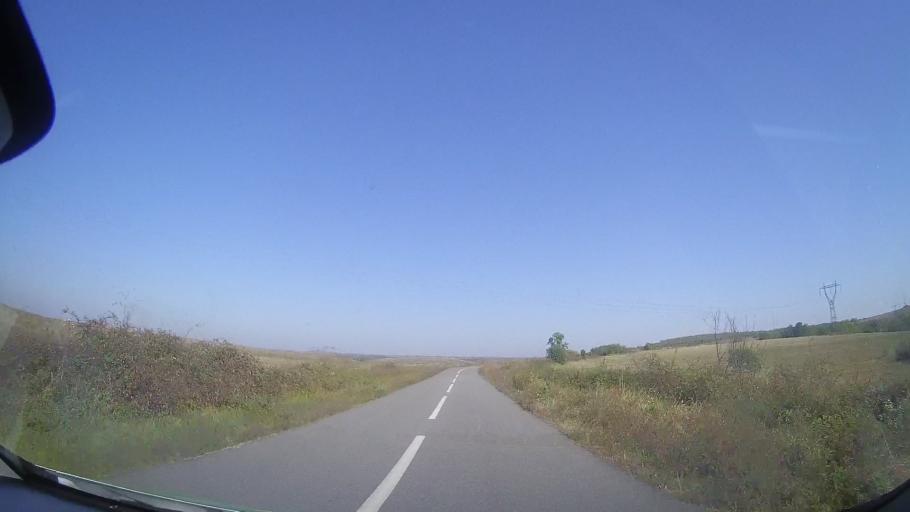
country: RO
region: Timis
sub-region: Comuna Balint
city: Balint
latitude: 45.8275
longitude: 21.8524
